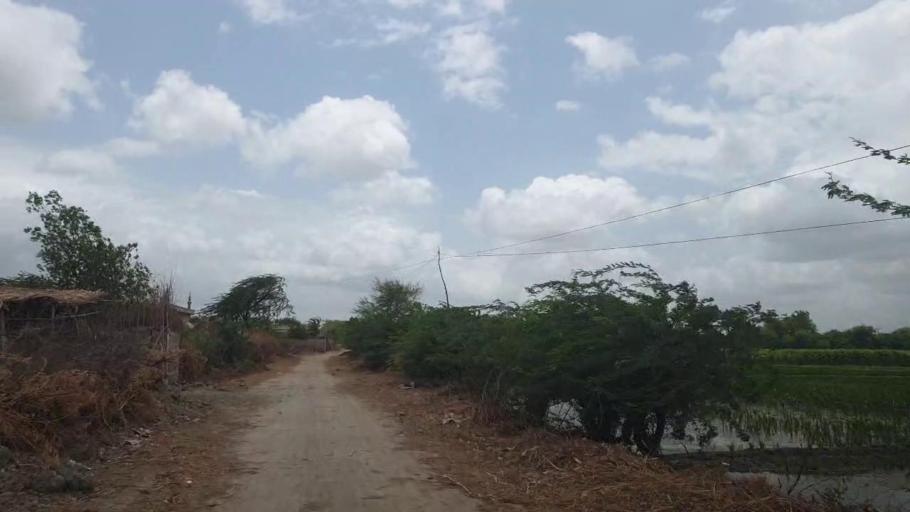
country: PK
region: Sindh
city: Badin
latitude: 24.6475
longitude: 68.9210
